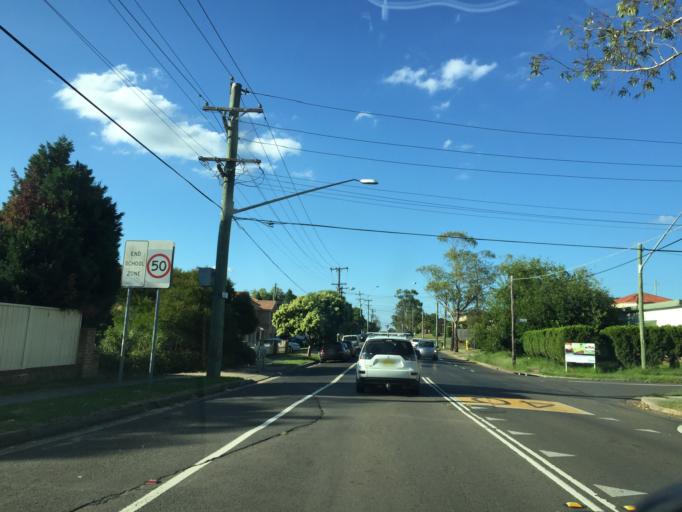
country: AU
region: New South Wales
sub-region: Blacktown
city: Blacktown
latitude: -33.7836
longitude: 150.8937
